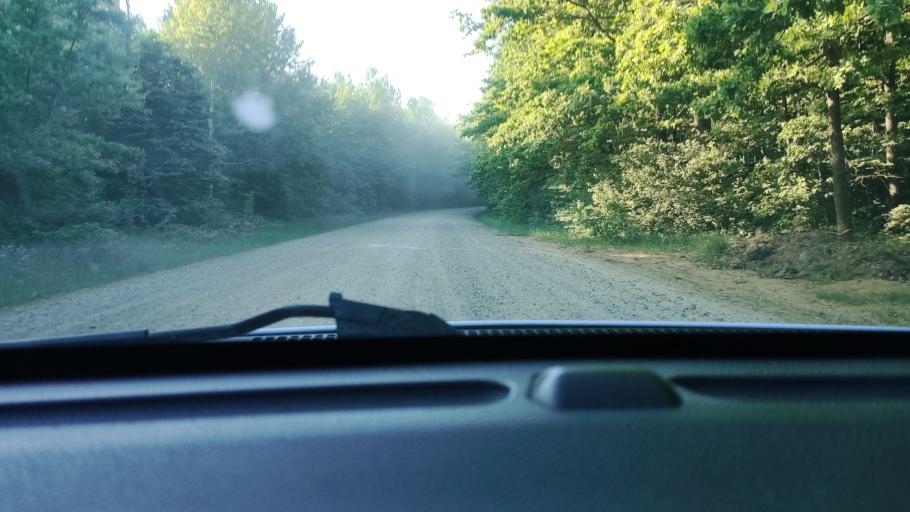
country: RU
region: Krasnodarskiy
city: Goryachiy Klyuch
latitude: 44.7126
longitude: 38.9914
